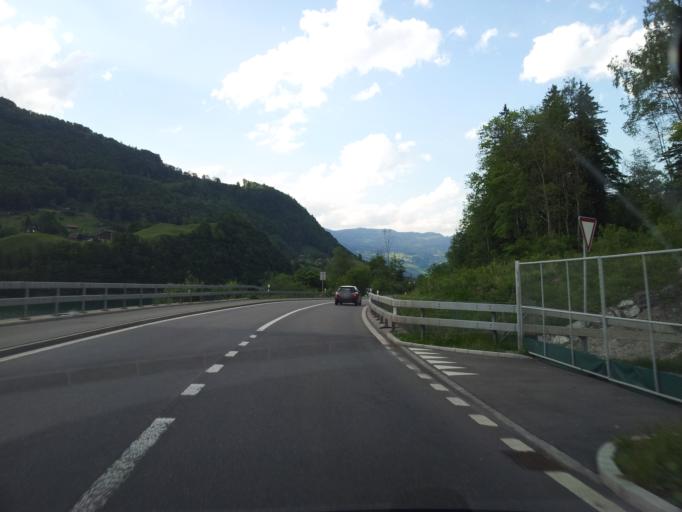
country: CH
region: Obwalden
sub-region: Obwalden
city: Lungern
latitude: 46.8039
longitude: 8.1692
